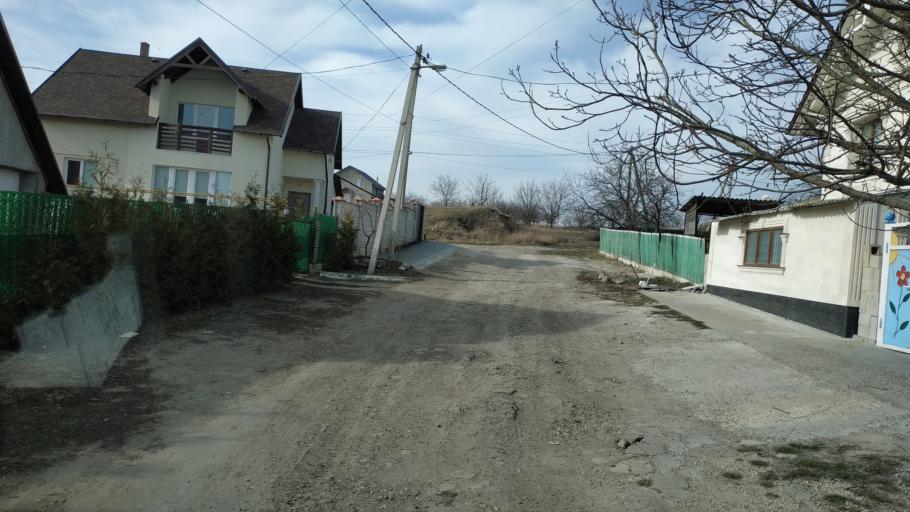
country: MD
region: Chisinau
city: Vatra
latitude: 47.0802
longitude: 28.6885
